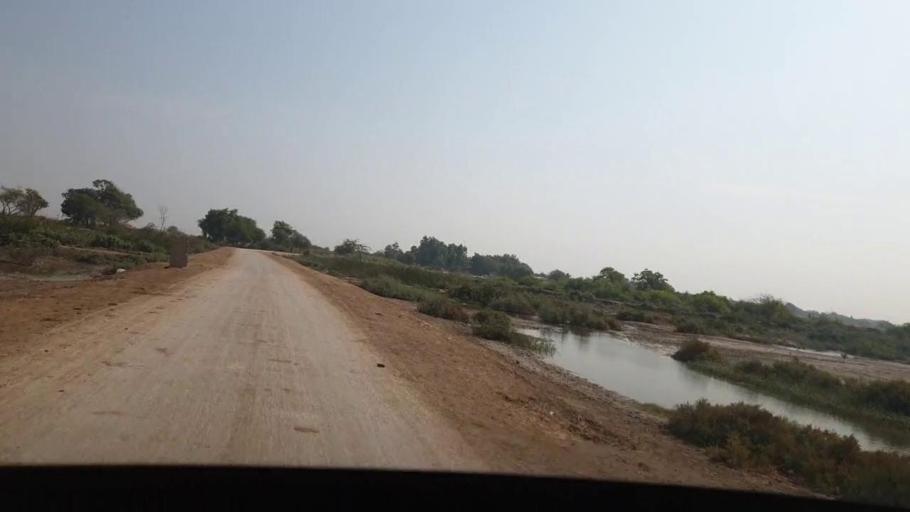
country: PK
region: Sindh
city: Chuhar Jamali
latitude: 24.2686
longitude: 67.9402
